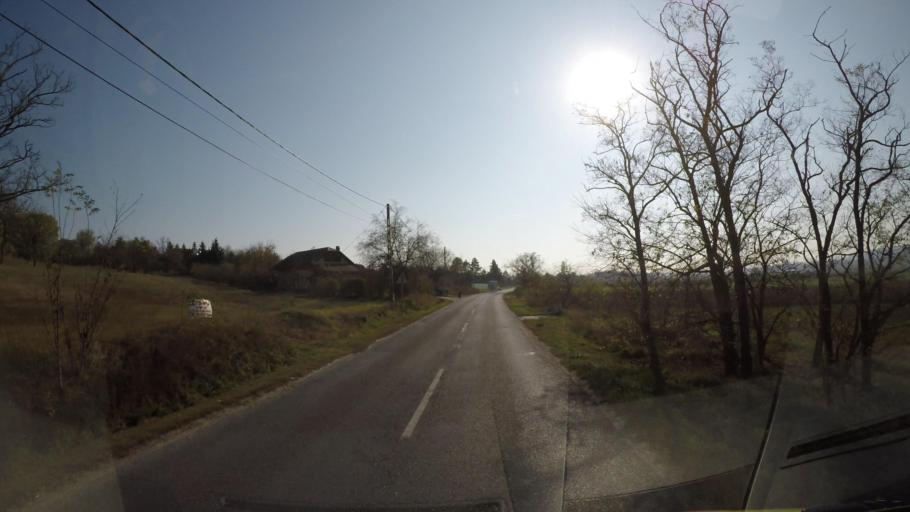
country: HU
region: Pest
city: Leanyfalu
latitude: 47.7072
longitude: 19.1072
